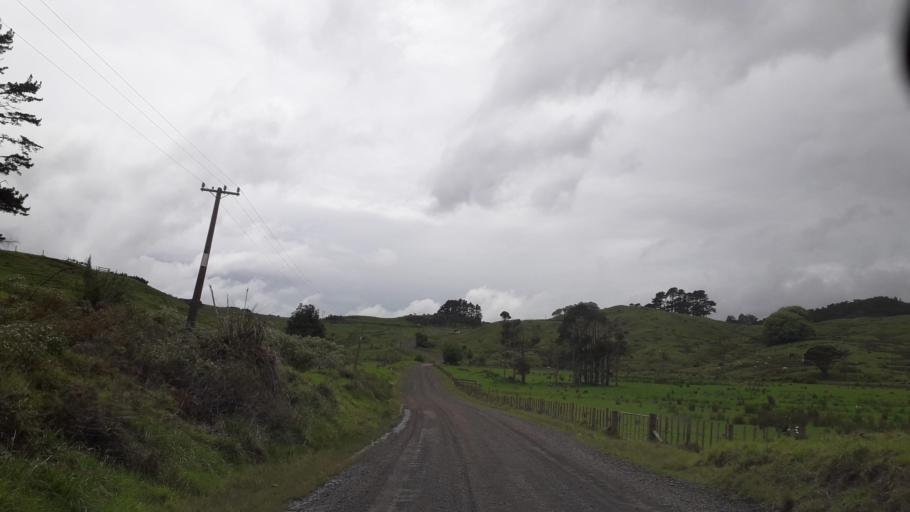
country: NZ
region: Northland
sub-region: Far North District
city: Ahipara
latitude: -35.4193
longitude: 173.3619
